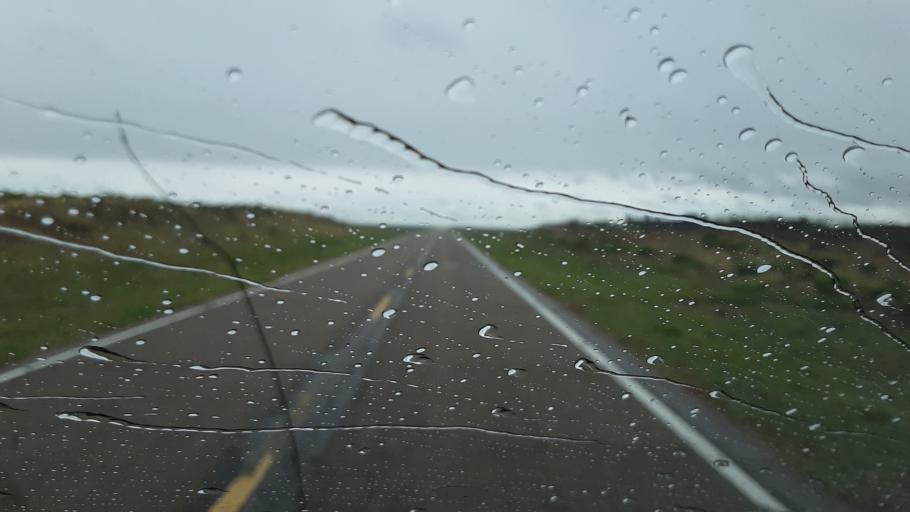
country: US
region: Colorado
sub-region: Lincoln County
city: Hugo
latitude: 38.8495
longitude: -103.2271
